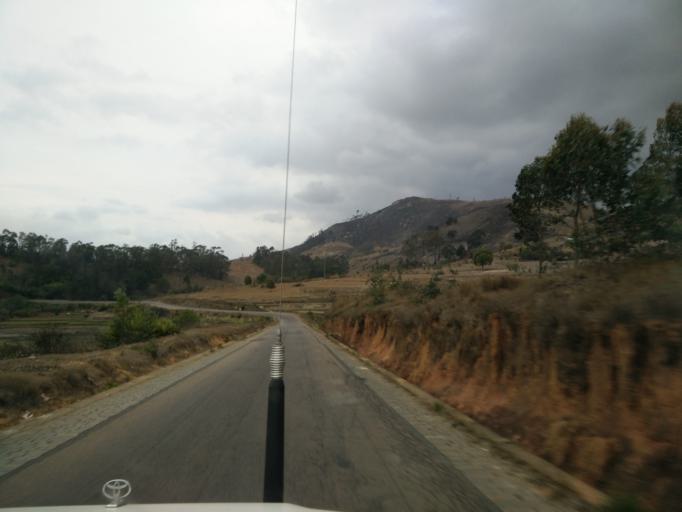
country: MG
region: Upper Matsiatra
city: Fianarantsoa
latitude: -21.5776
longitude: 47.0334
